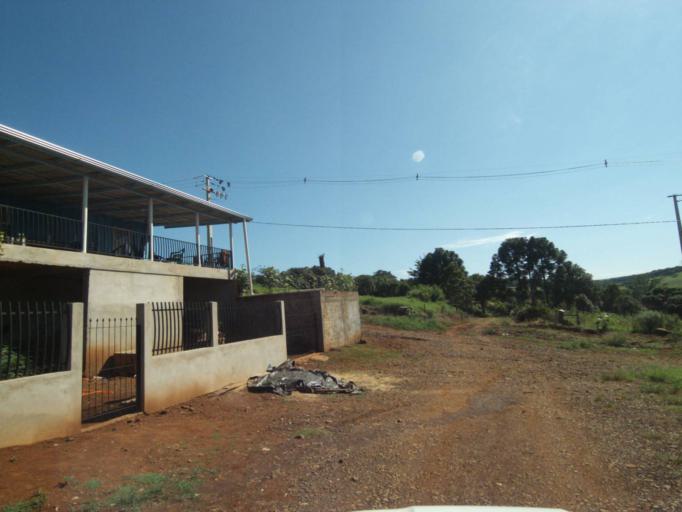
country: BR
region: Parana
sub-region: Laranjeiras Do Sul
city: Laranjeiras do Sul
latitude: -25.4919
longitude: -52.5234
